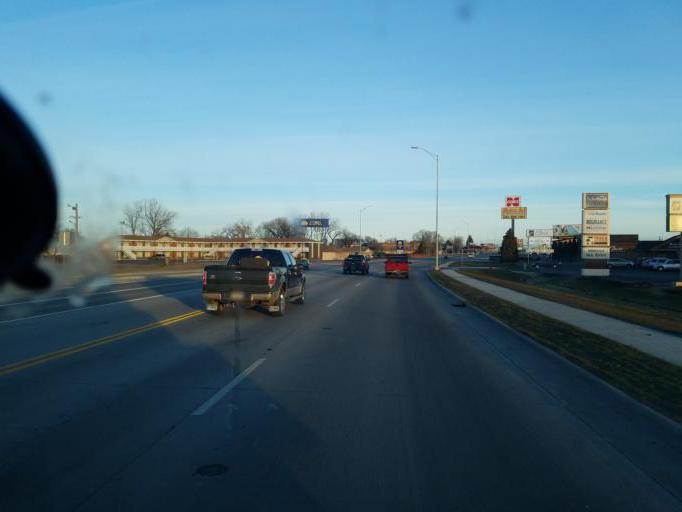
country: US
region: South Dakota
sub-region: Davison County
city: Mitchell
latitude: 43.6985
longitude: -98.0176
